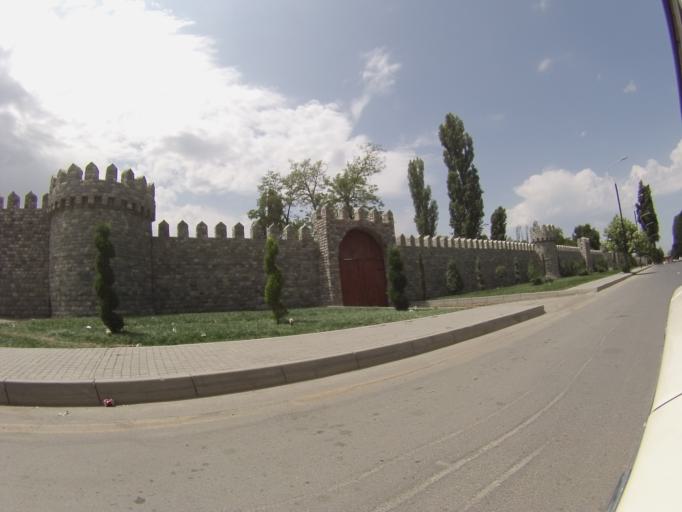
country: AZ
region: Ismayilli
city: Ismayilli
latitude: 40.7855
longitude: 48.1777
